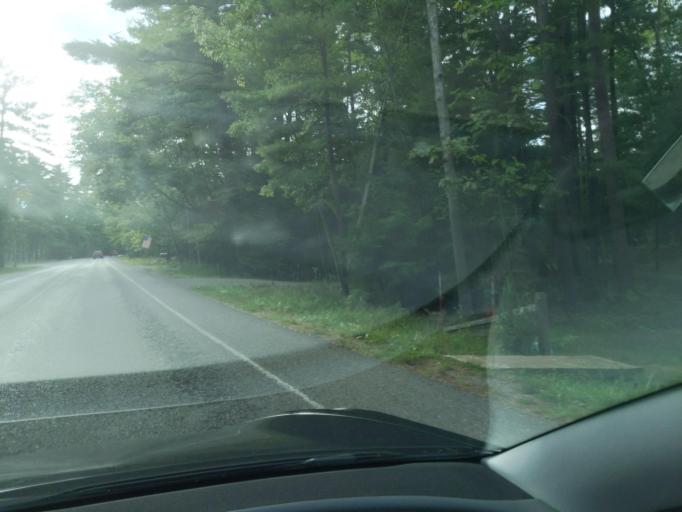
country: US
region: Michigan
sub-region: Kalkaska County
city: Rapid City
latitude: 44.8525
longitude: -85.3151
